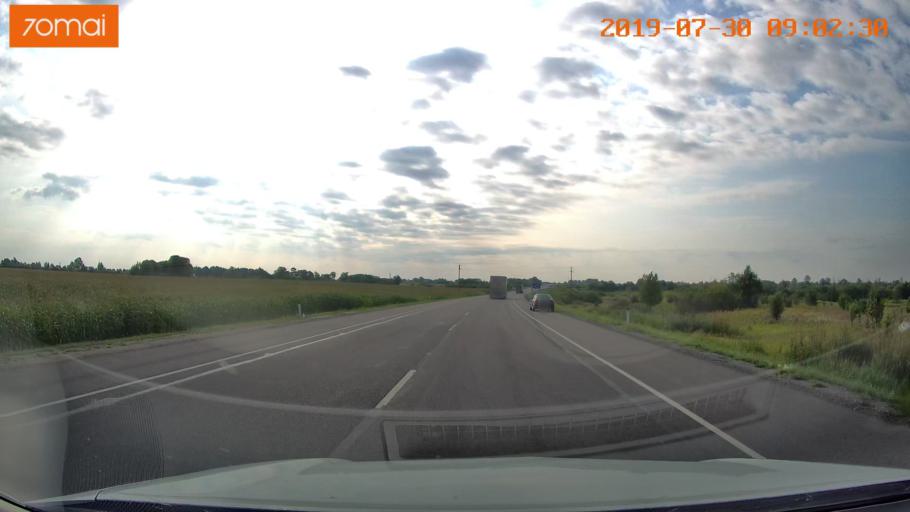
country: RU
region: Kaliningrad
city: Gusev
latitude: 54.6155
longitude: 22.2335
